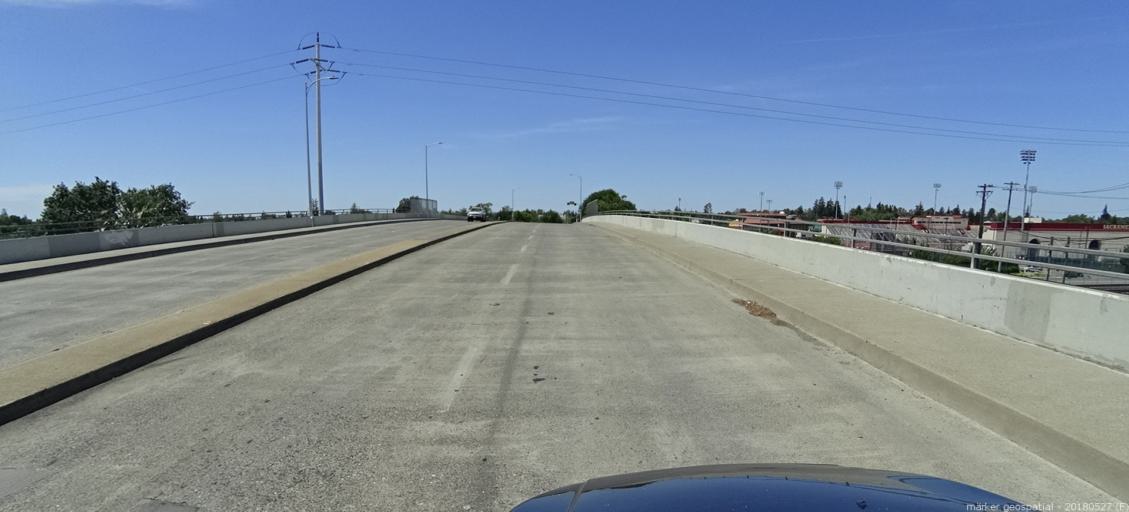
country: US
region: California
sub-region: Sacramento County
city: Sacramento
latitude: 38.5398
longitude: -121.4836
